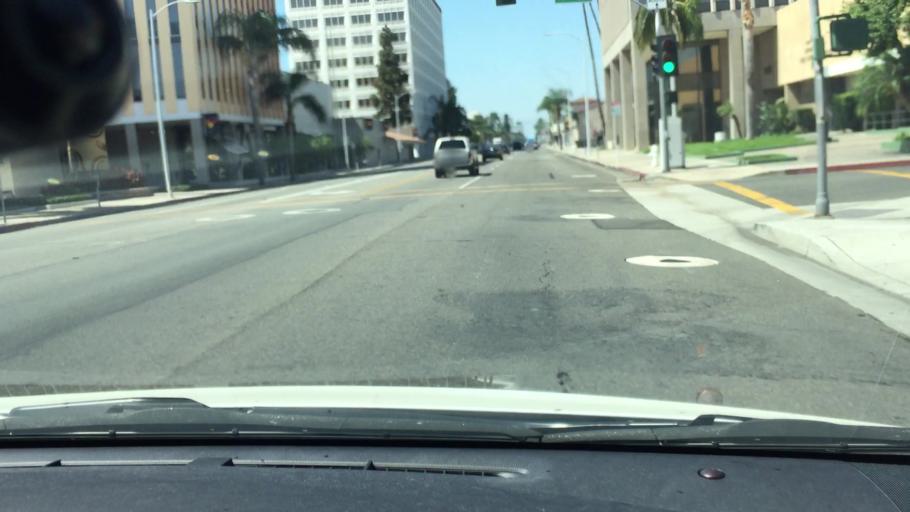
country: US
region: California
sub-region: Orange County
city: Santa Ana
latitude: 33.7534
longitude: -117.8676
